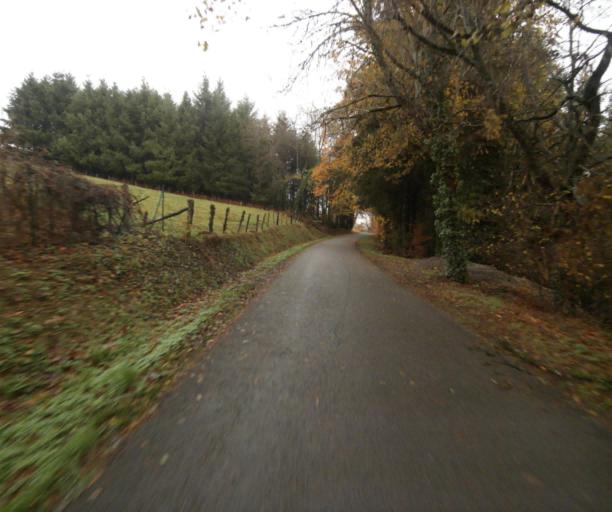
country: FR
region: Limousin
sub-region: Departement de la Correze
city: Cornil
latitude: 45.1959
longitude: 1.6423
